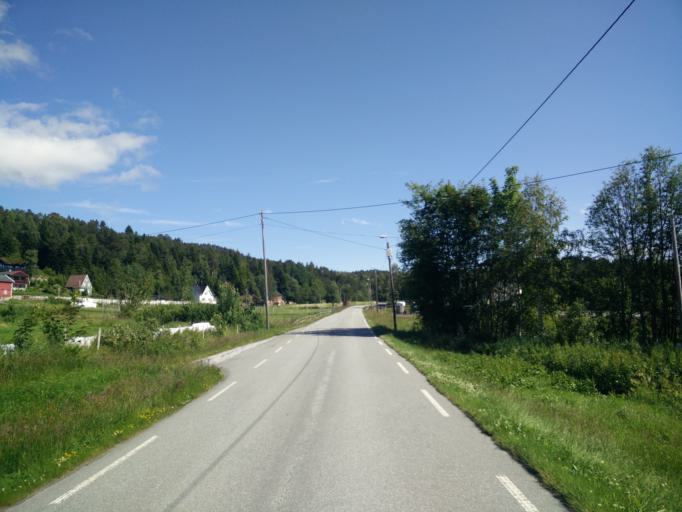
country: NO
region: More og Romsdal
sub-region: Kristiansund
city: Rensvik
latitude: 63.0357
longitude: 7.8240
